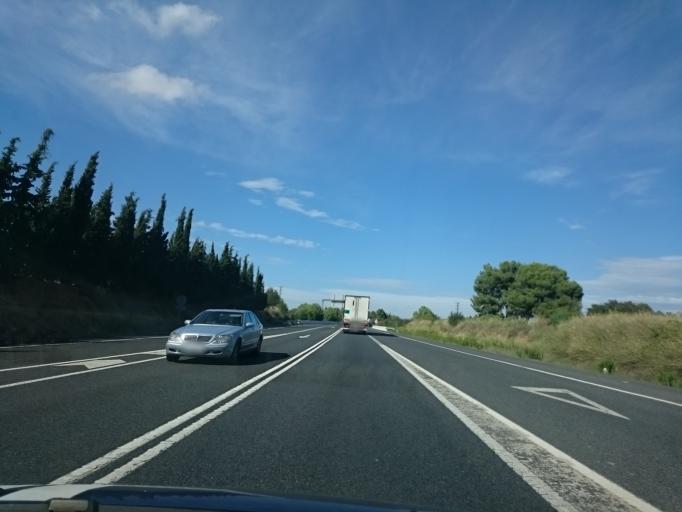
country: ES
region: Catalonia
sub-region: Provincia de Barcelona
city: Castellet
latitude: 41.3138
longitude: 1.6405
